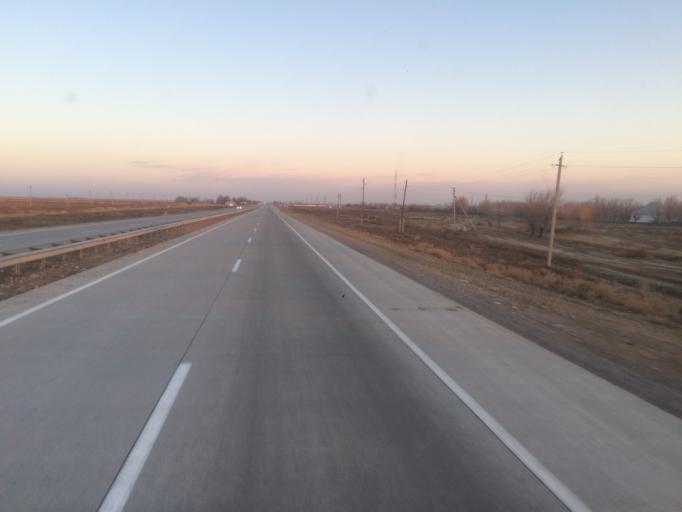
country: KZ
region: Ongtustik Qazaqstan
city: Bayaldyr
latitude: 43.0654
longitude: 68.6753
